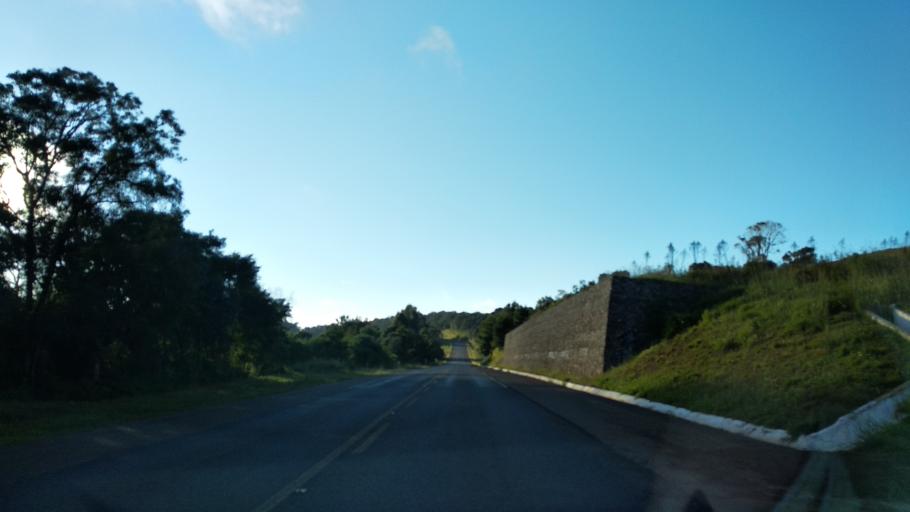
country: BR
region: Santa Catarina
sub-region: Correia Pinto
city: Correia Pinto
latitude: -27.6150
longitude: -50.6891
